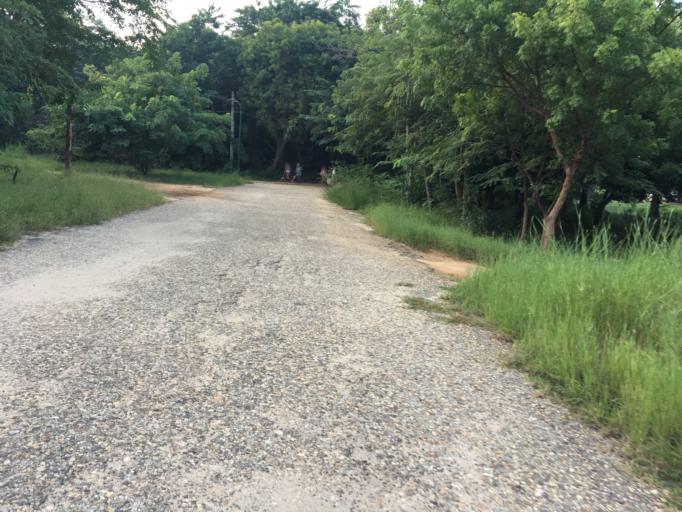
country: MM
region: Magway
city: Pakokku
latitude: 21.1795
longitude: 94.9047
